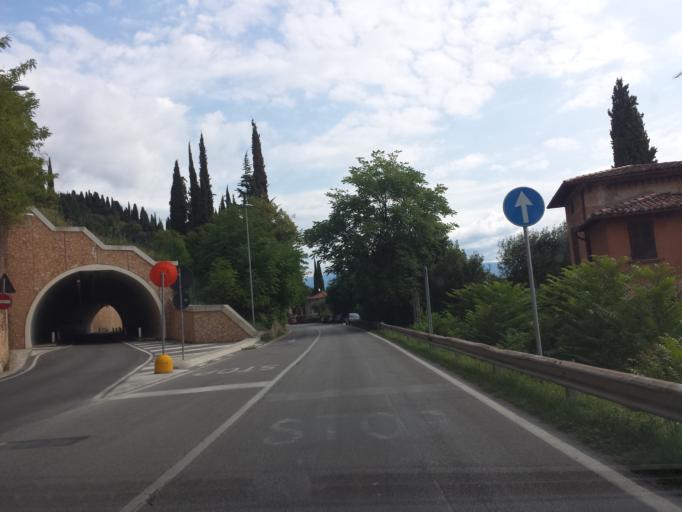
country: IT
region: Lombardy
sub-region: Provincia di Brescia
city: Salo
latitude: 45.6107
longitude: 10.5384
